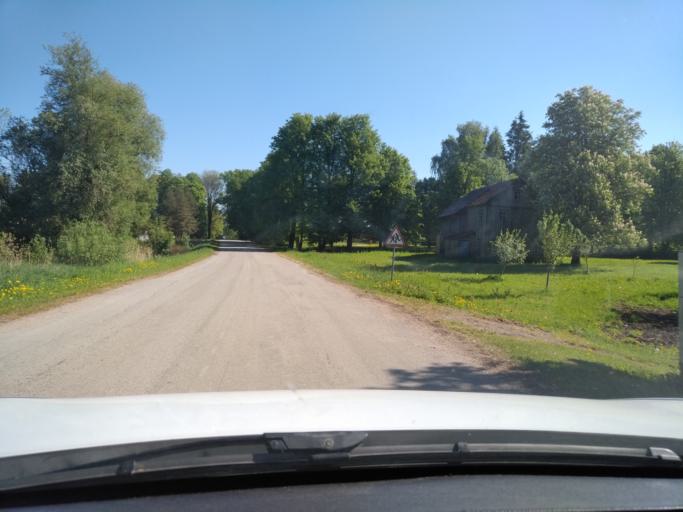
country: LT
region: Panevezys
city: Rokiskis
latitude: 55.7409
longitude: 25.5224
